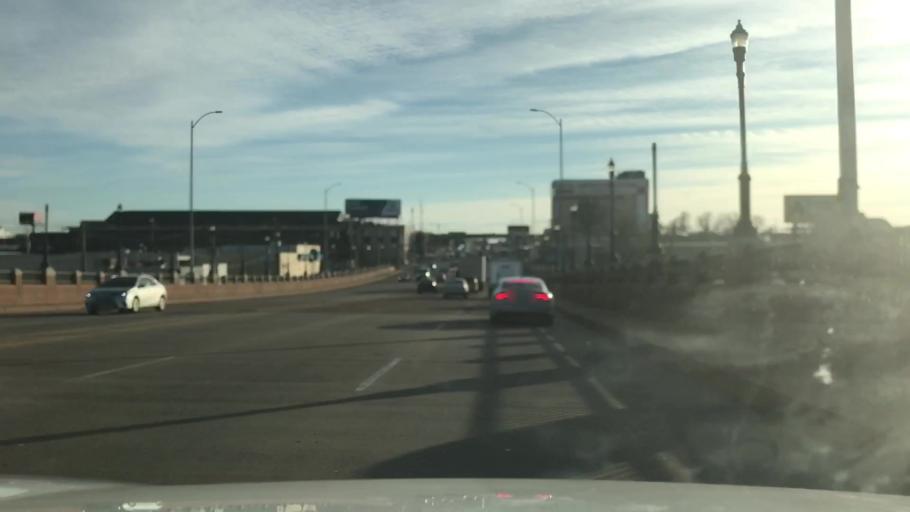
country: US
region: Missouri
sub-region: Saint Louis County
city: Richmond Heights
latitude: 38.6225
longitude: -90.2658
